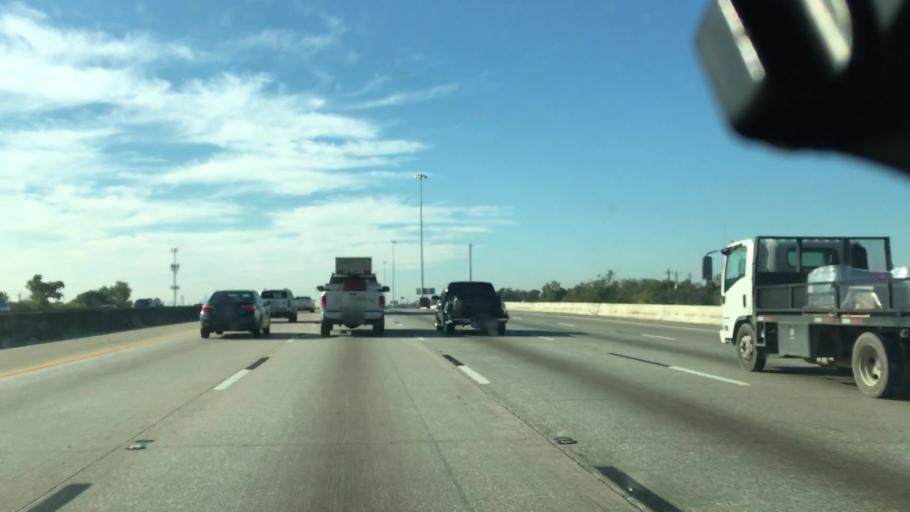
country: US
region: Texas
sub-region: Harris County
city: Aldine
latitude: 29.8809
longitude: -95.3241
